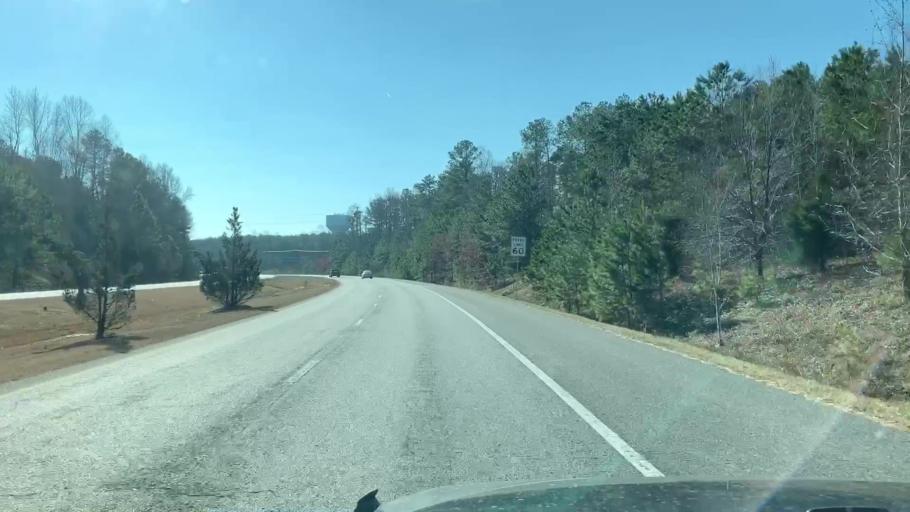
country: US
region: Virginia
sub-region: James City County
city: Williamsburg
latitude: 37.3302
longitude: -76.7557
